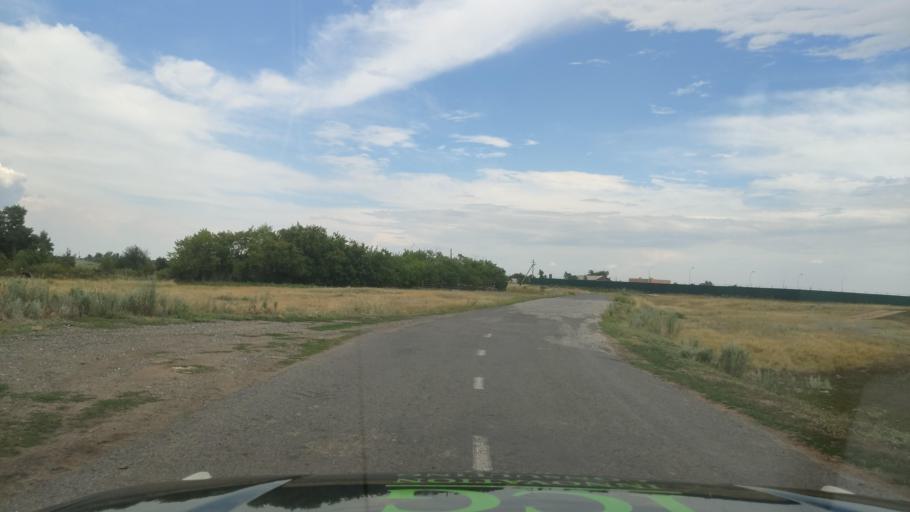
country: KZ
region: Pavlodar
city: Pavlodar
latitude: 52.6612
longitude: 77.4966
